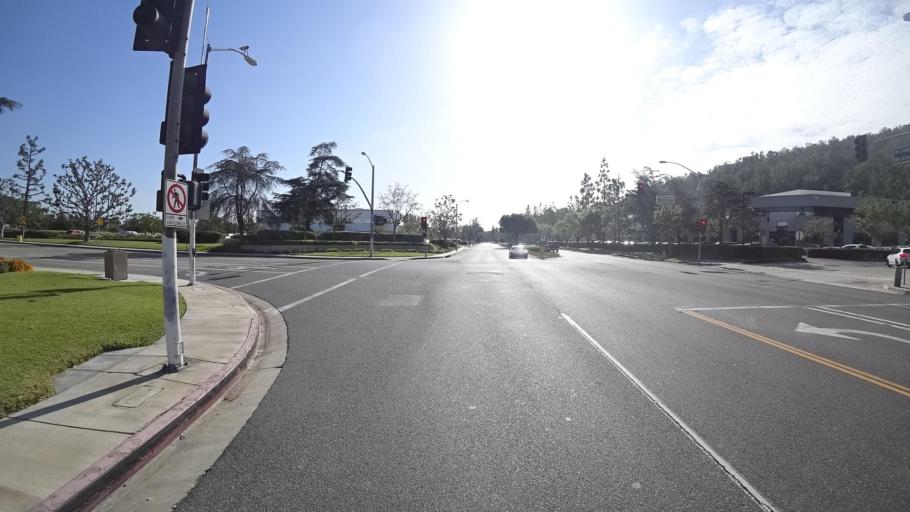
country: US
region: California
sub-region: Los Angeles County
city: South El Monte
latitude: 34.0289
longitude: -118.0261
